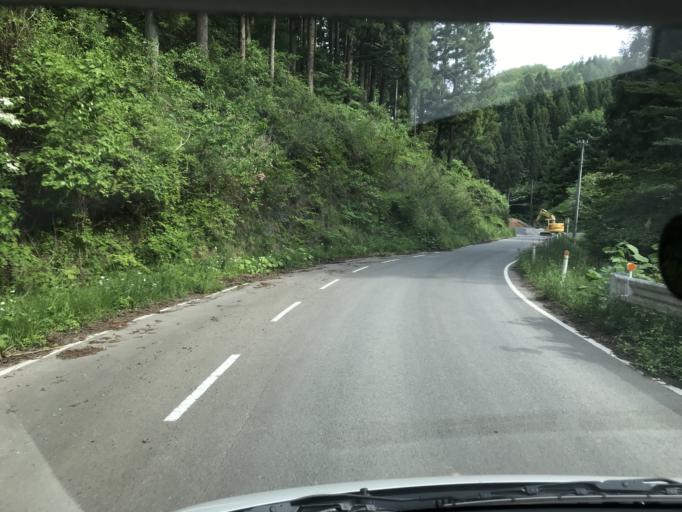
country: JP
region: Miyagi
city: Wakuya
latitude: 38.6839
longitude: 141.3458
